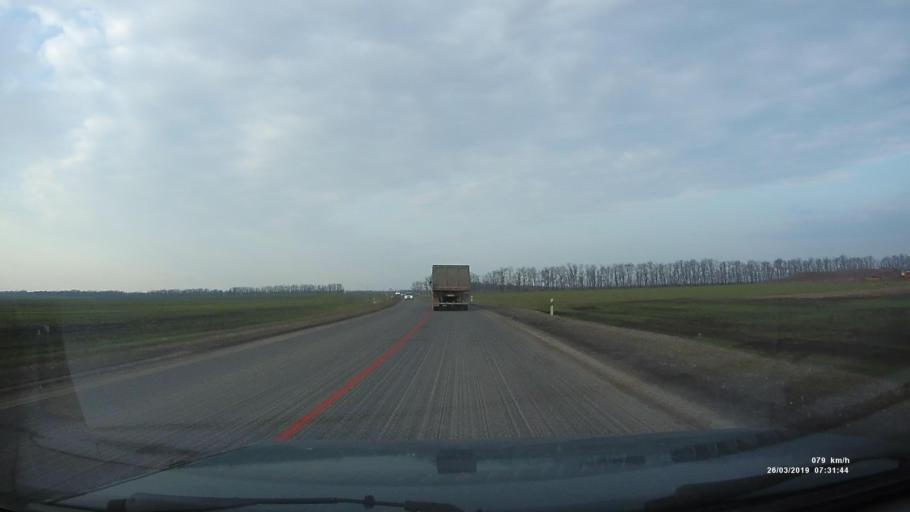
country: RU
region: Rostov
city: Novobessergenovka
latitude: 47.2312
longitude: 38.7868
